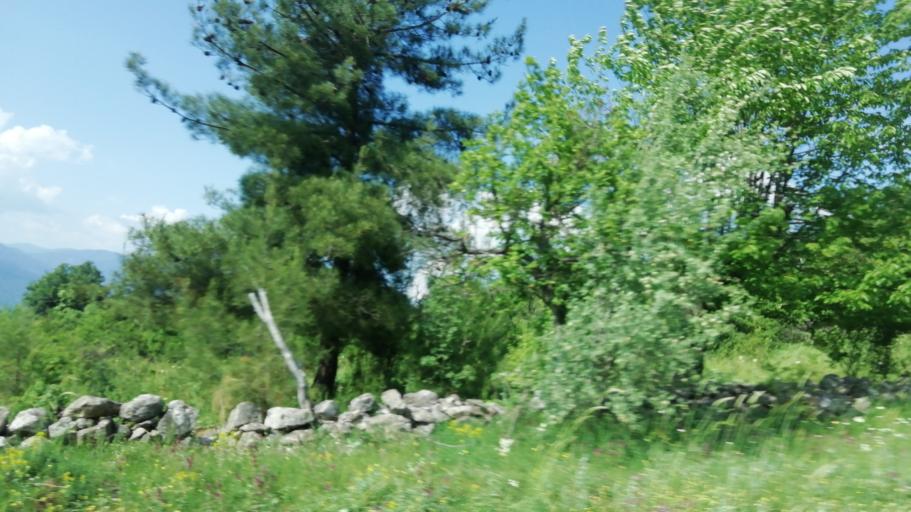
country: TR
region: Karabuk
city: Karabuk
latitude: 41.1253
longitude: 32.5796
